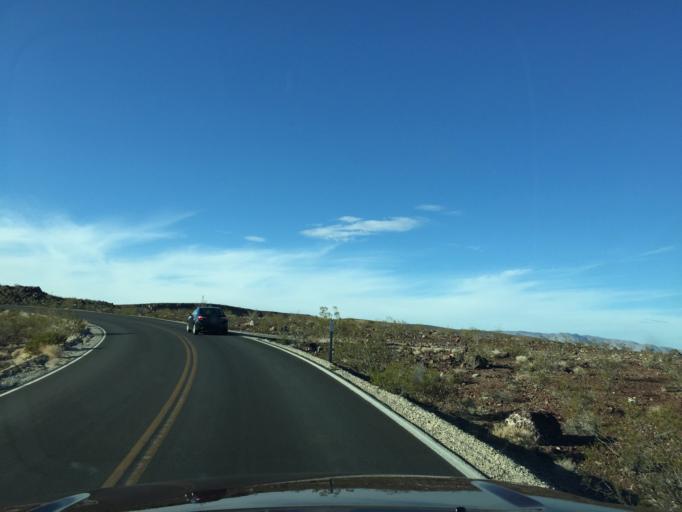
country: US
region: California
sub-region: Inyo County
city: Lone Pine
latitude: 36.3459
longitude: -117.5407
